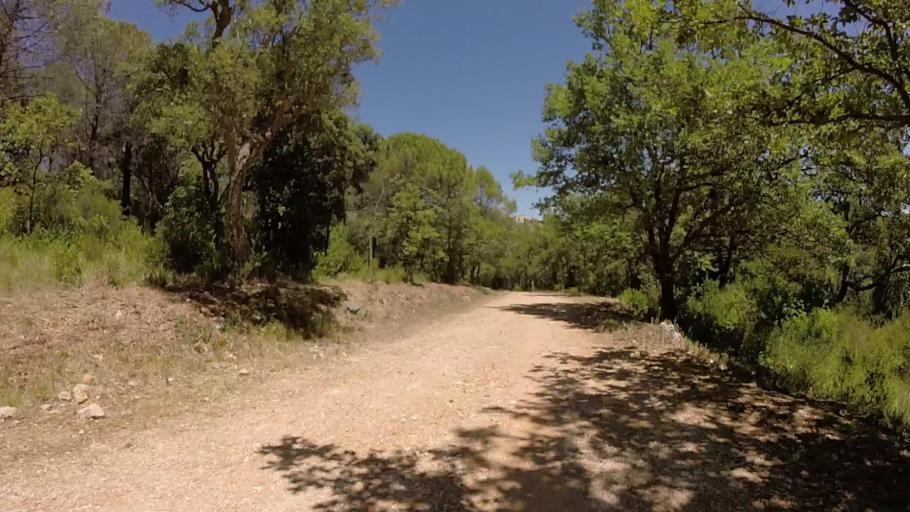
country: FR
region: Provence-Alpes-Cote d'Azur
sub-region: Departement des Alpes-Maritimes
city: Valbonne
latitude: 43.6335
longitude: 7.0361
